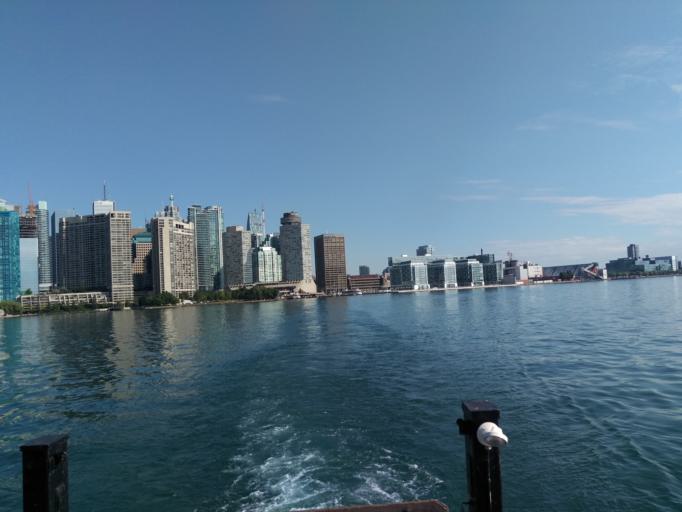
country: CA
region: Ontario
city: Toronto
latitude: 43.6336
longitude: -79.3754
